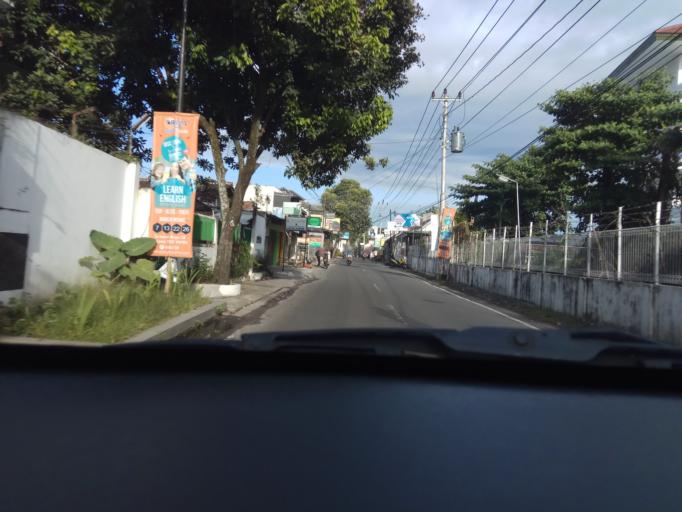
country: ID
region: Daerah Istimewa Yogyakarta
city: Depok
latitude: -7.7636
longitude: 110.4077
